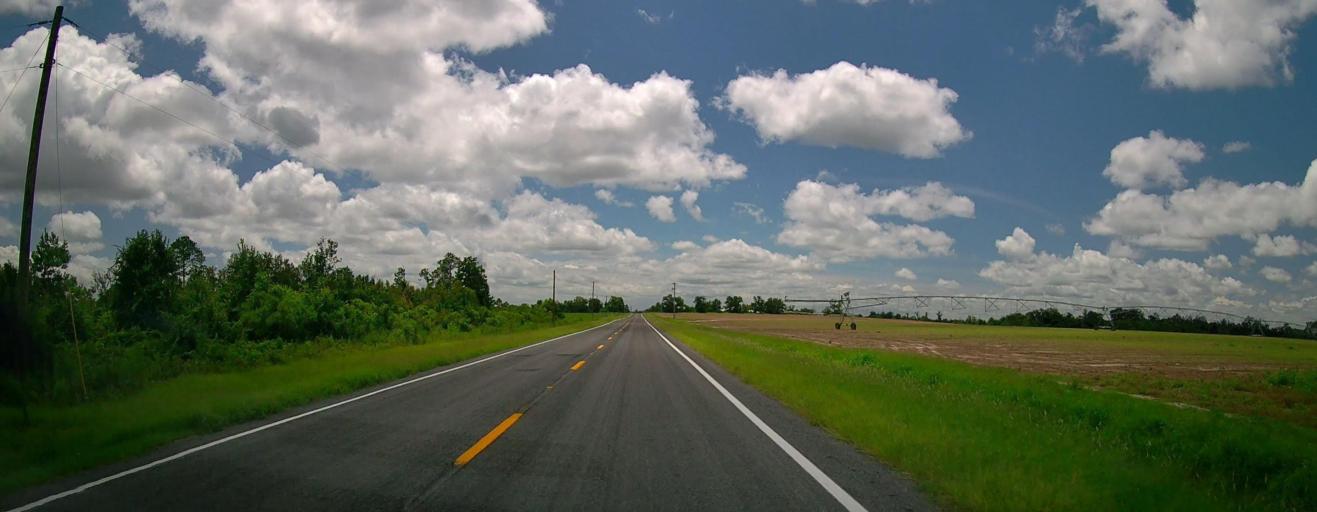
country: US
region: Georgia
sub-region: Turner County
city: Ashburn
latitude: 31.8140
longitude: -83.5696
